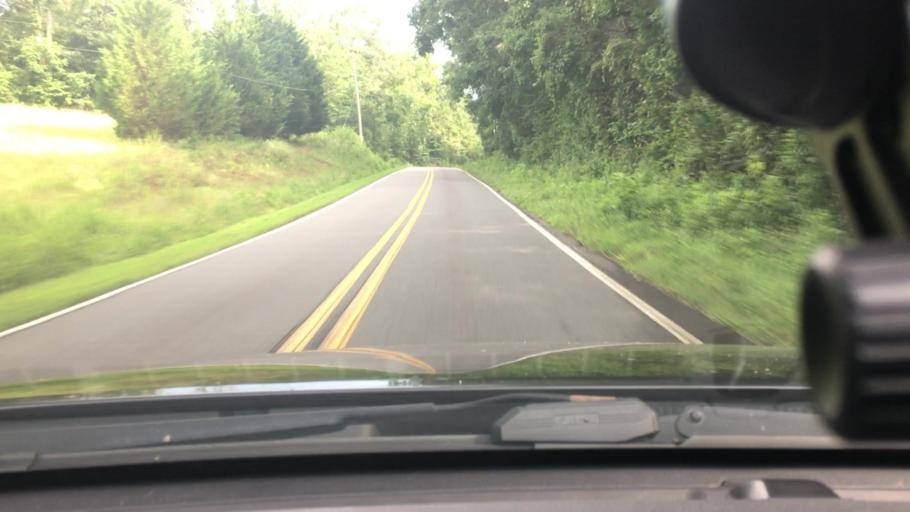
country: US
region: North Carolina
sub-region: Rutherford County
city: Rutherfordton
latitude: 35.3934
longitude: -81.9709
